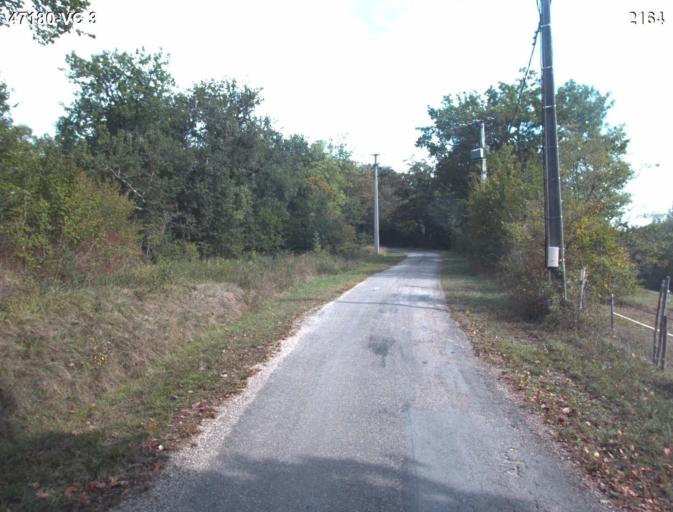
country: FR
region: Aquitaine
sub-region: Departement du Lot-et-Garonne
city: Sainte-Colombe-en-Bruilhois
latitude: 44.1516
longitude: 0.4417
